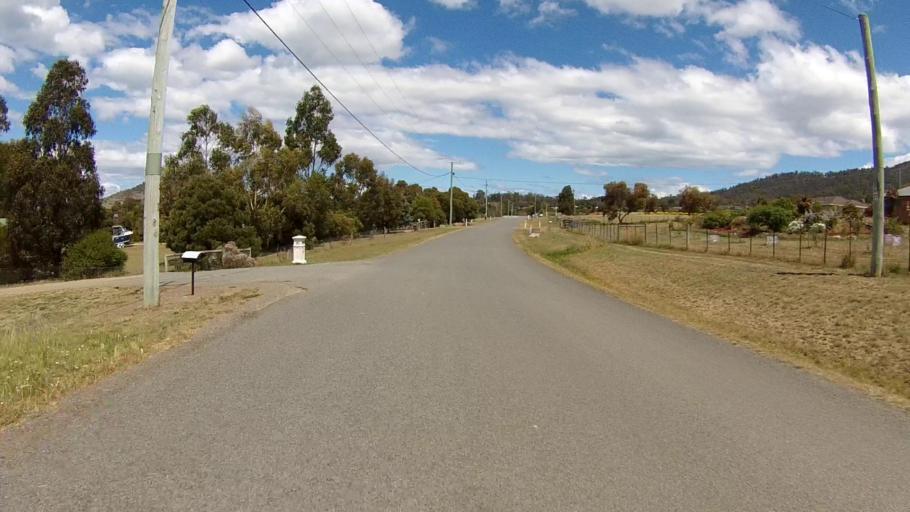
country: AU
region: Tasmania
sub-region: Clarence
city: Seven Mile Beach
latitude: -42.8509
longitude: 147.4800
